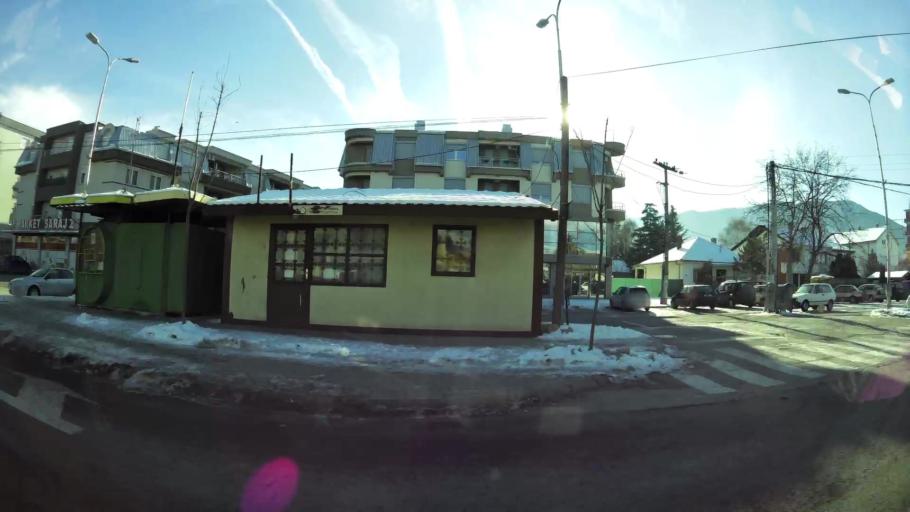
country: MK
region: Saraj
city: Saraj
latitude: 41.9976
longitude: 21.3257
